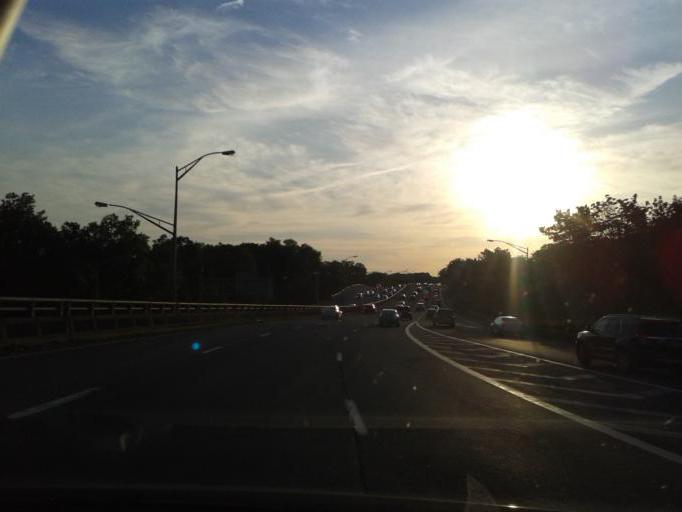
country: US
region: New York
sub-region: Westchester County
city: Pelham
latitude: 40.9222
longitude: -73.8181
